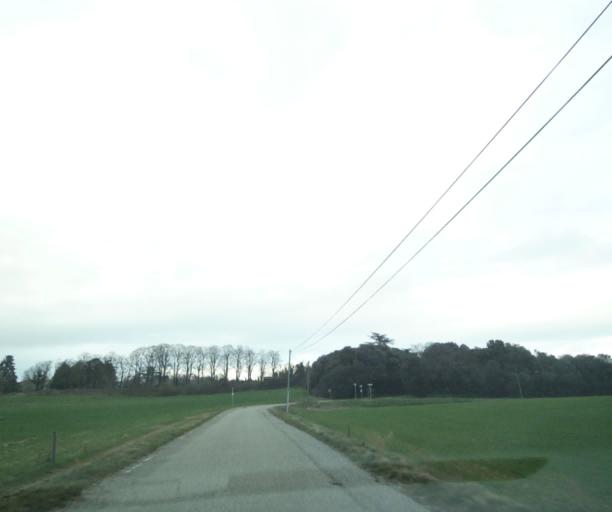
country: FR
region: Rhone-Alpes
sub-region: Departement de la Drome
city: Bourg-les-Valence
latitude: 44.9785
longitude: 4.9044
